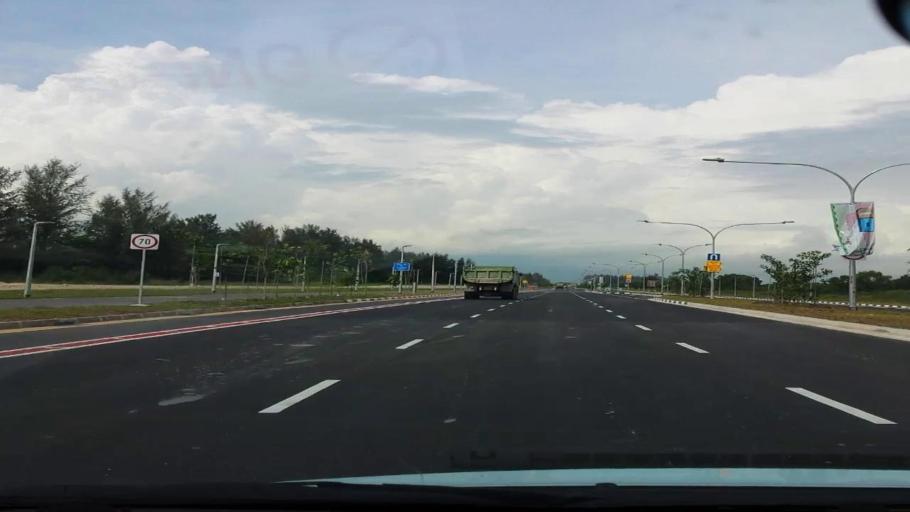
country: SG
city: Singapore
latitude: 1.3404
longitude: 104.0251
